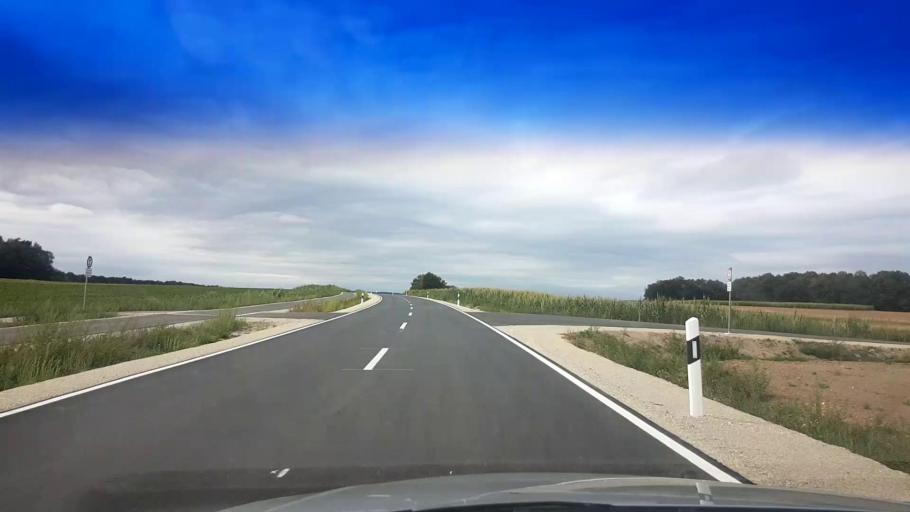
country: DE
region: Bavaria
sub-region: Upper Franconia
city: Frensdorf
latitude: 49.8018
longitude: 10.8758
